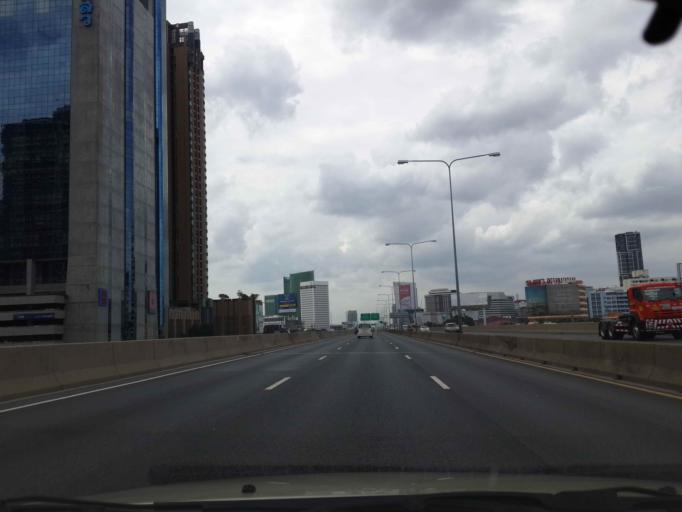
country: TH
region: Bangkok
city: Chatuchak
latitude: 13.8069
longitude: 100.5599
